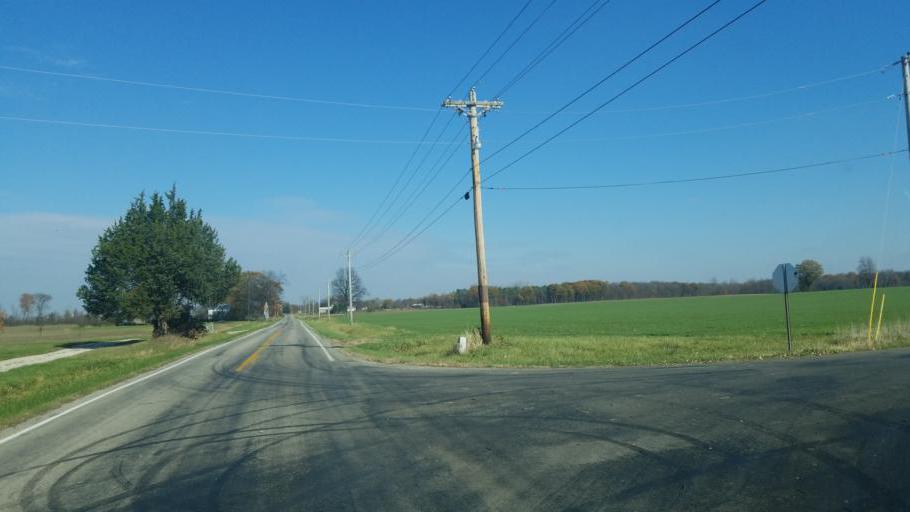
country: US
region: Ohio
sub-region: Lorain County
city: Camden
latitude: 41.2101
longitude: -82.2620
